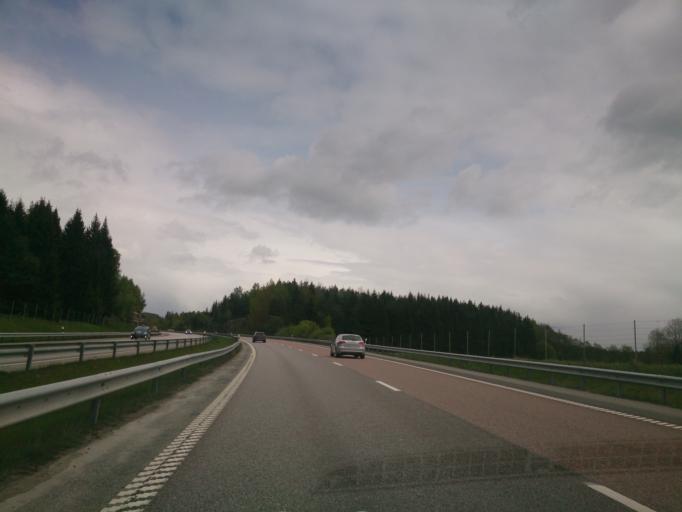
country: SE
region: Stockholm
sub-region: Sodertalje Kommun
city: Pershagen
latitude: 59.1204
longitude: 17.6275
